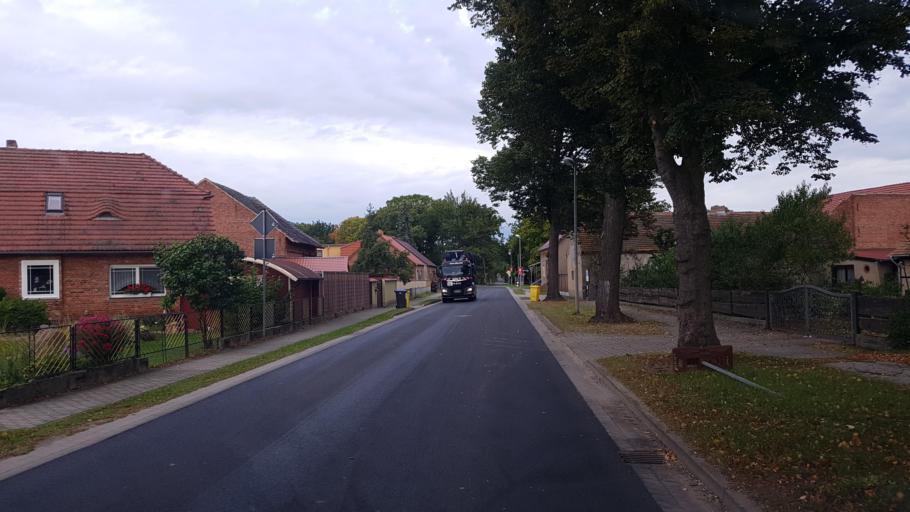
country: DE
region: Brandenburg
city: Kasel-Golzig
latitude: 51.9341
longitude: 13.6939
